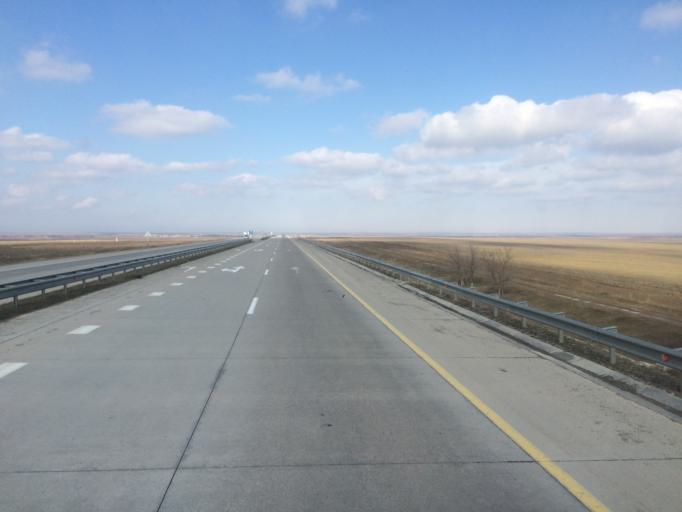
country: KZ
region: Ongtustik Qazaqstan
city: Temirlanovka
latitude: 42.7329
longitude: 69.2081
